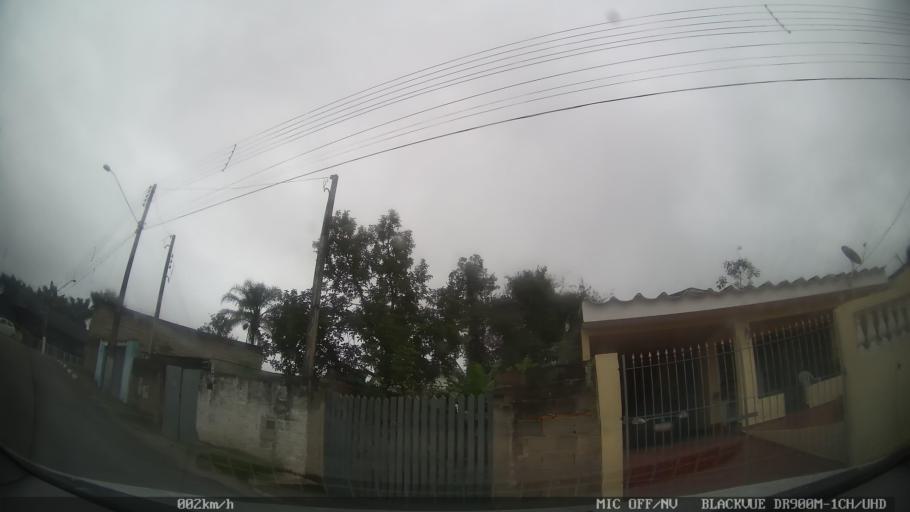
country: BR
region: Sao Paulo
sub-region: Juquia
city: Juquia
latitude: -24.3252
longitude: -47.6312
